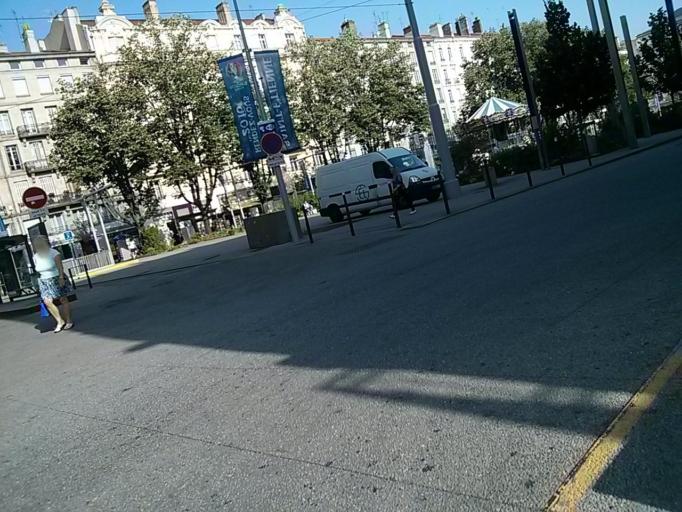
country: FR
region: Rhone-Alpes
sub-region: Departement de la Loire
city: Saint-Etienne
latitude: 45.4385
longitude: 4.3881
